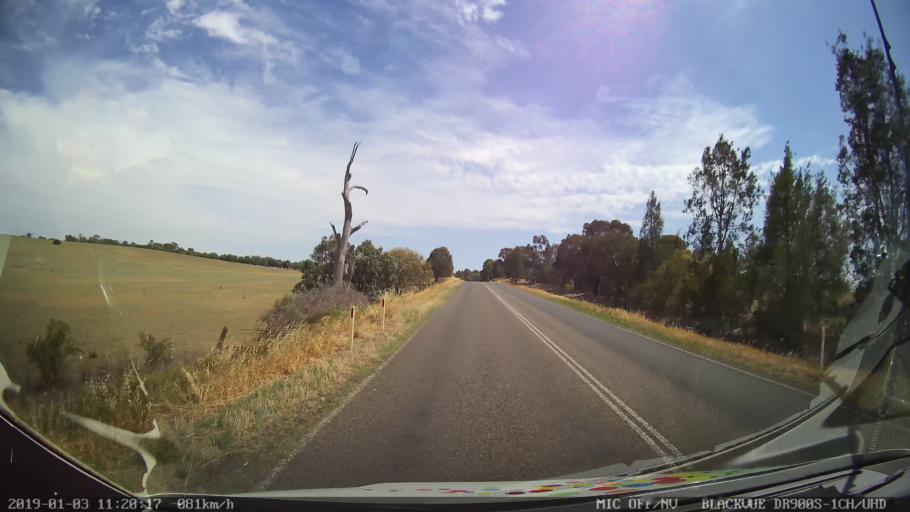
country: AU
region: New South Wales
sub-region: Young
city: Young
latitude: -34.1029
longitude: 148.2550
